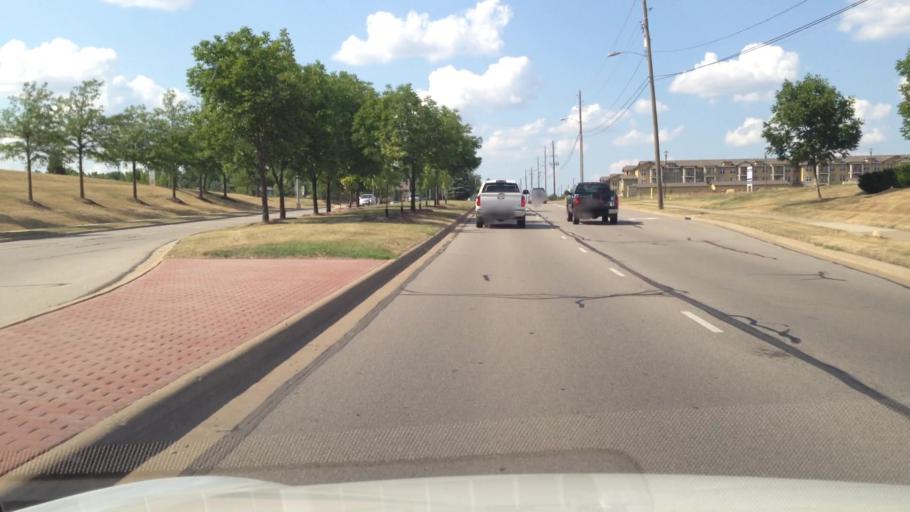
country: US
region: Kansas
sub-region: Johnson County
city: Olathe
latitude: 38.9135
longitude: -94.7973
